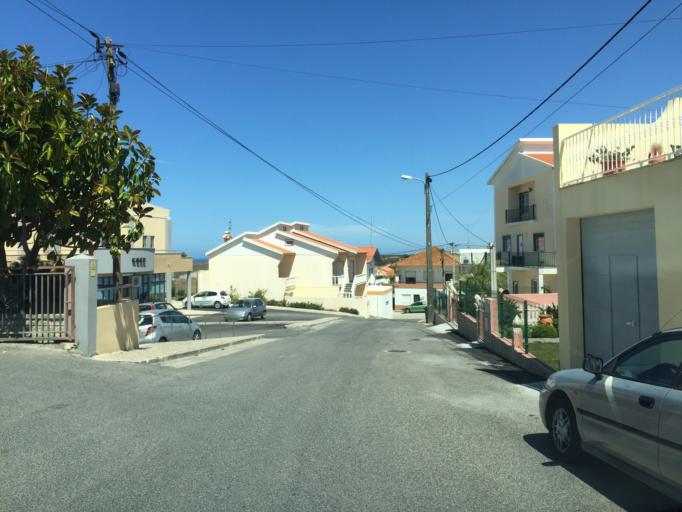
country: PT
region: Lisbon
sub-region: Lourinha
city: Lourinha
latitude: 39.2024
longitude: -9.3306
